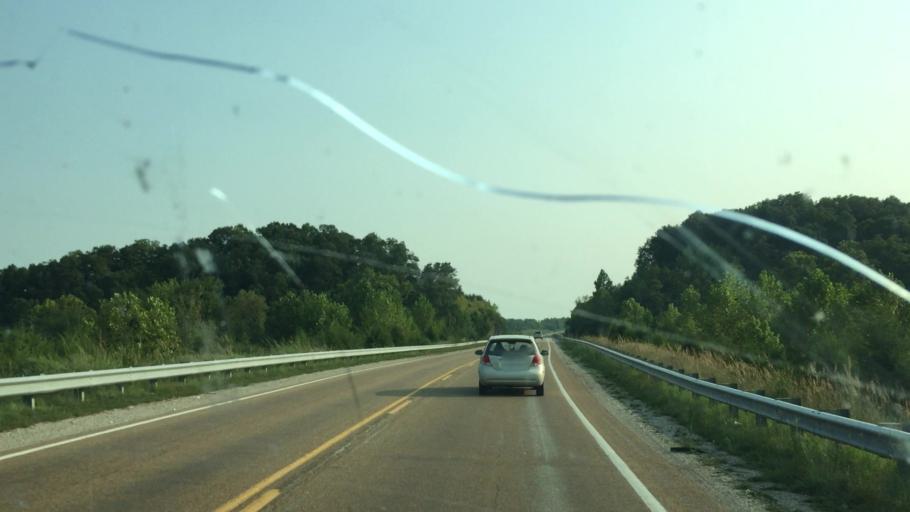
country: US
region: Missouri
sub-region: Pulaski County
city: Richland
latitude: 37.8024
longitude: -92.4051
